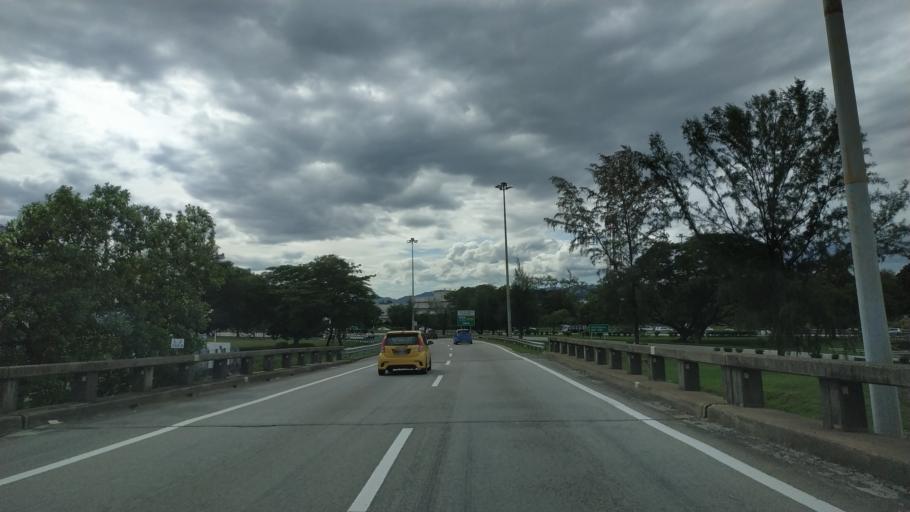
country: MY
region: Penang
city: Perai
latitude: 5.3635
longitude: 100.3980
